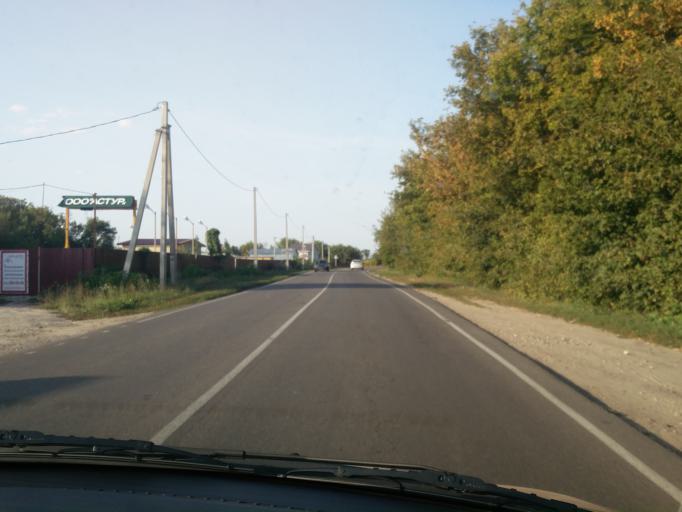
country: RU
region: Voronezj
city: Ramon'
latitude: 51.9178
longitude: 39.3204
